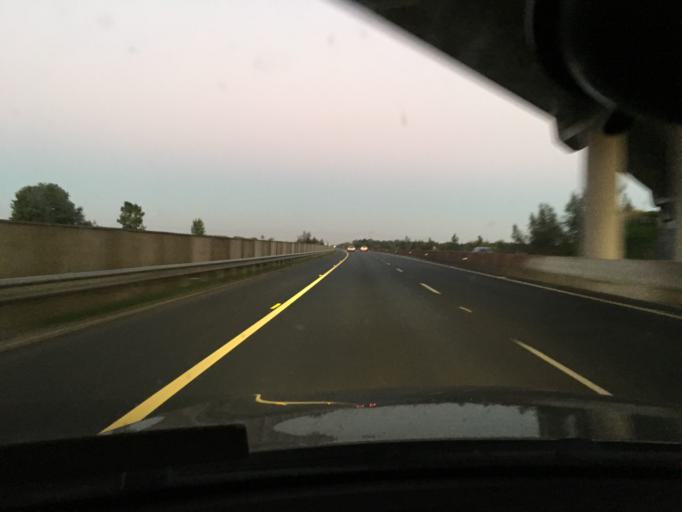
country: IE
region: Connaught
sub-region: County Galway
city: Athenry
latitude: 53.2763
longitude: -8.7188
